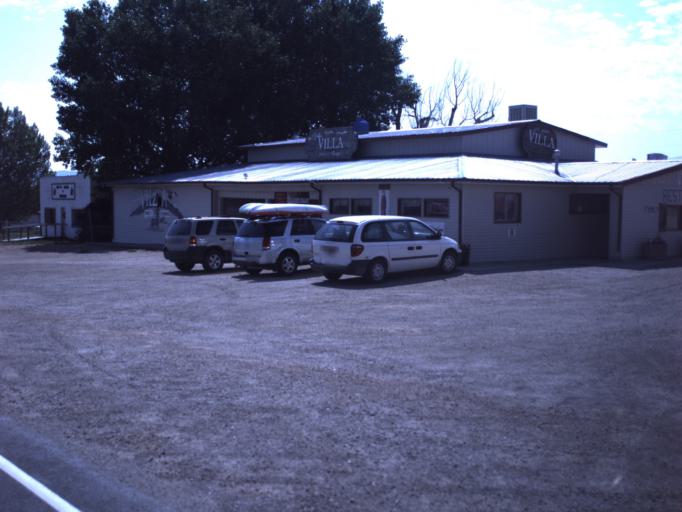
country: US
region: Utah
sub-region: Daggett County
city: Manila
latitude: 40.9883
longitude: -109.7173
